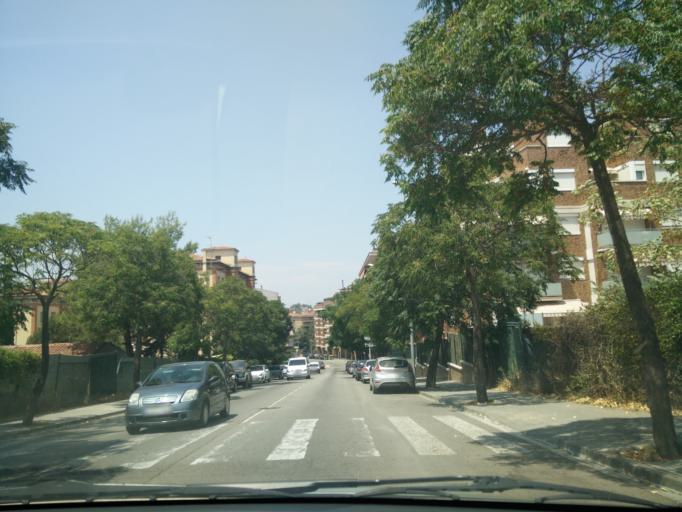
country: ES
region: Catalonia
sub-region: Provincia de Barcelona
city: Manresa
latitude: 41.7255
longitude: 1.8399
